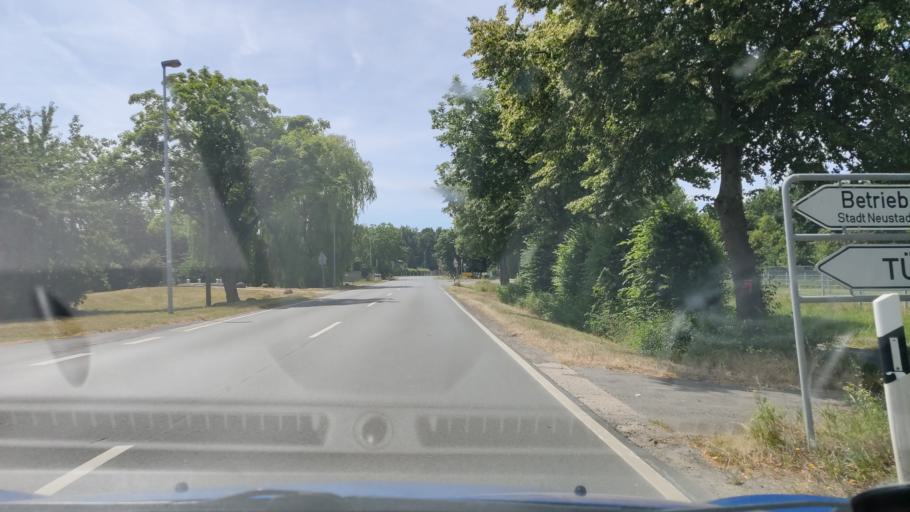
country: DE
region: Lower Saxony
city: Neustadt am Rubenberge
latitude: 52.5151
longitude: 9.4650
